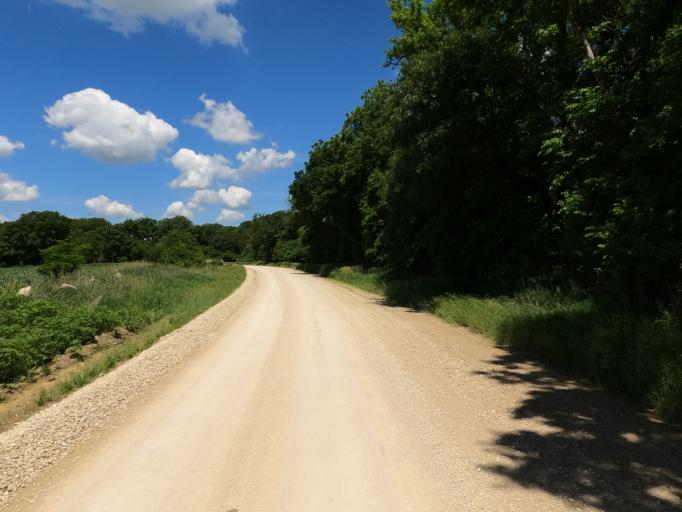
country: US
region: Kansas
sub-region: Marion County
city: Marion
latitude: 38.2440
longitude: -96.8069
